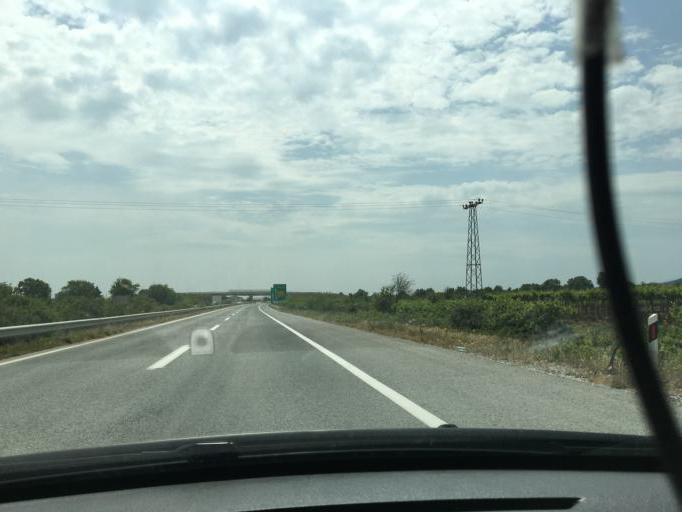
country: MK
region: Gevgelija
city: Gevgelija
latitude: 41.2161
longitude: 22.4919
